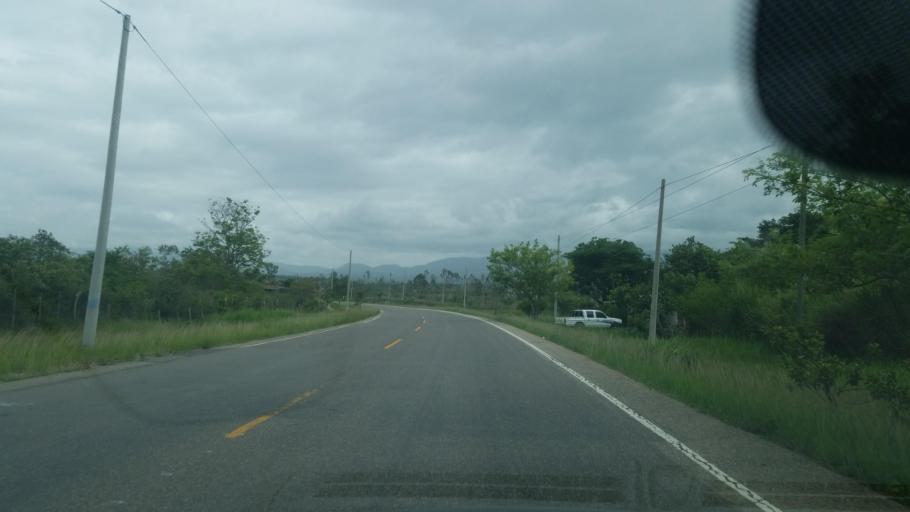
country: HN
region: Ocotepeque
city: Lucerna
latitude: 14.5307
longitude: -88.9509
